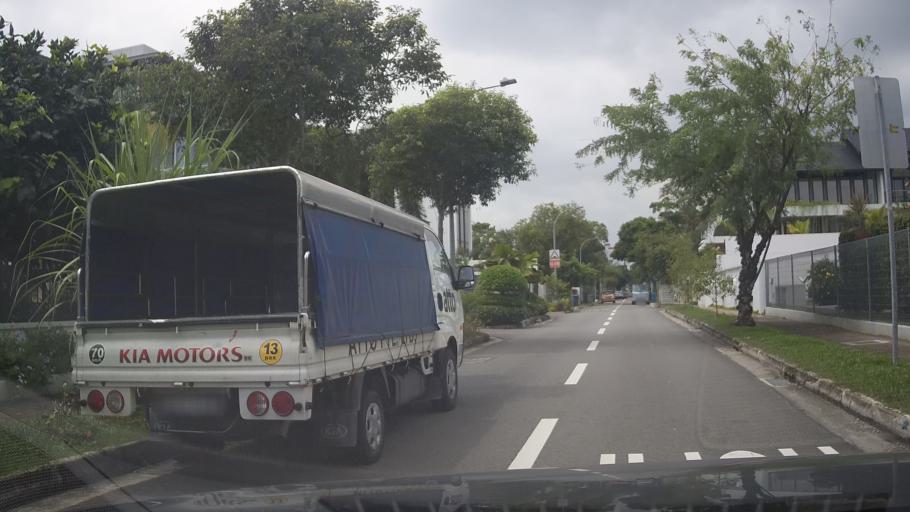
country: SG
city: Singapore
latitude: 1.3034
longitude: 103.8894
